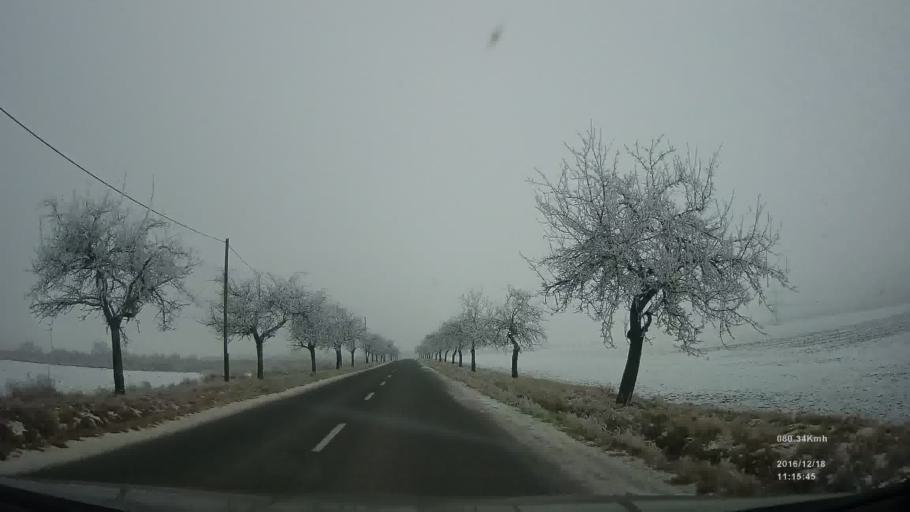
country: SK
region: Presovsky
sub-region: Okres Presov
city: Presov
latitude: 48.9091
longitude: 21.3248
